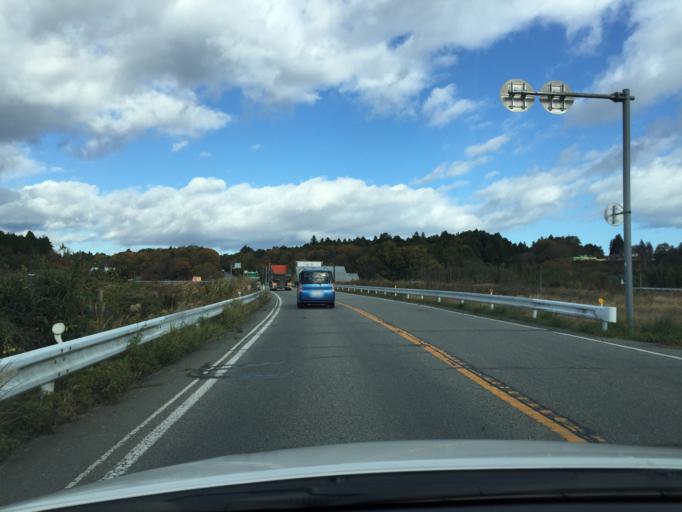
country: JP
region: Fukushima
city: Namie
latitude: 37.3867
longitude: 141.0085
